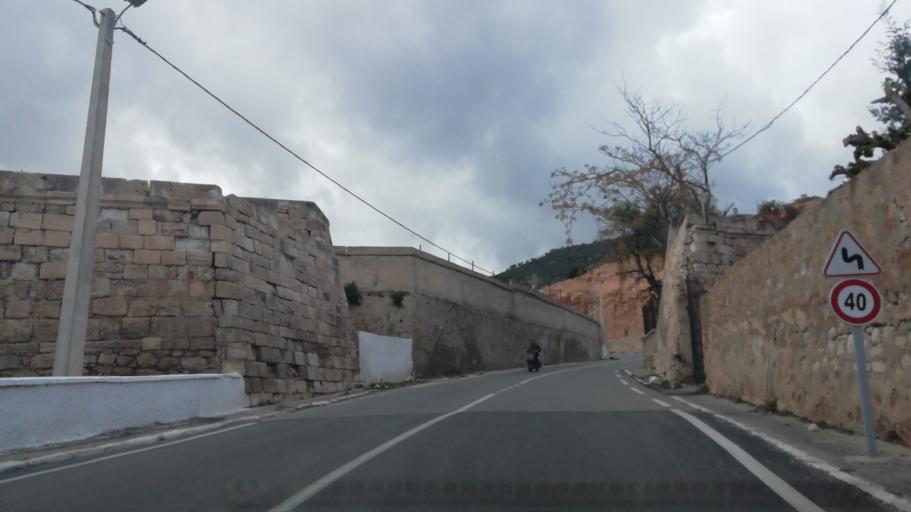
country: DZ
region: Oran
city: Oran
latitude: 35.7055
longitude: -0.6563
